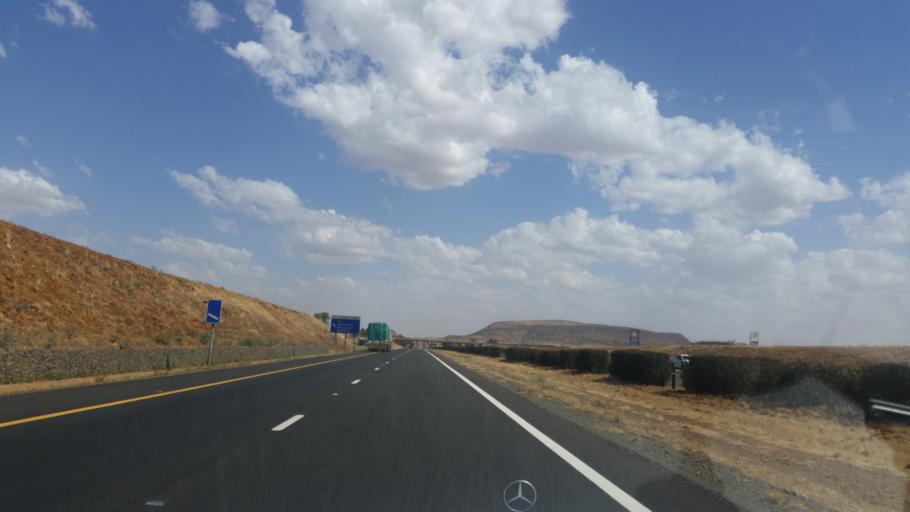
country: ZA
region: Orange Free State
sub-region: Mangaung Metropolitan Municipality
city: Bloemfontein
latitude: -29.1961
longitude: 26.1925
